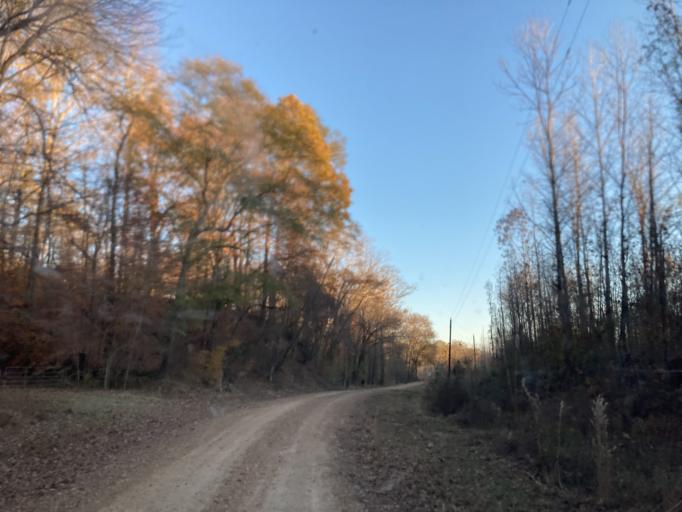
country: US
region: Mississippi
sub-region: Yazoo County
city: Yazoo City
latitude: 32.9716
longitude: -90.2625
